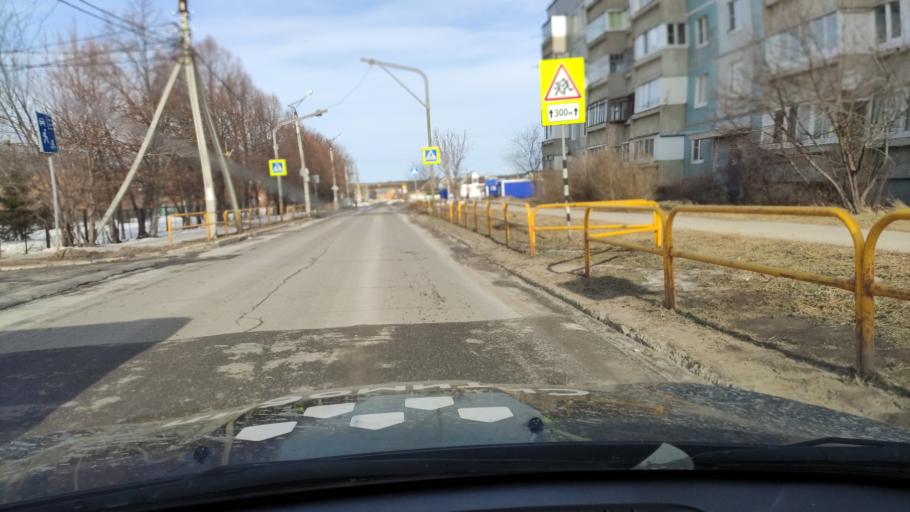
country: RU
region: Samara
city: Povolzhskiy
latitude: 53.5902
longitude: 49.7612
